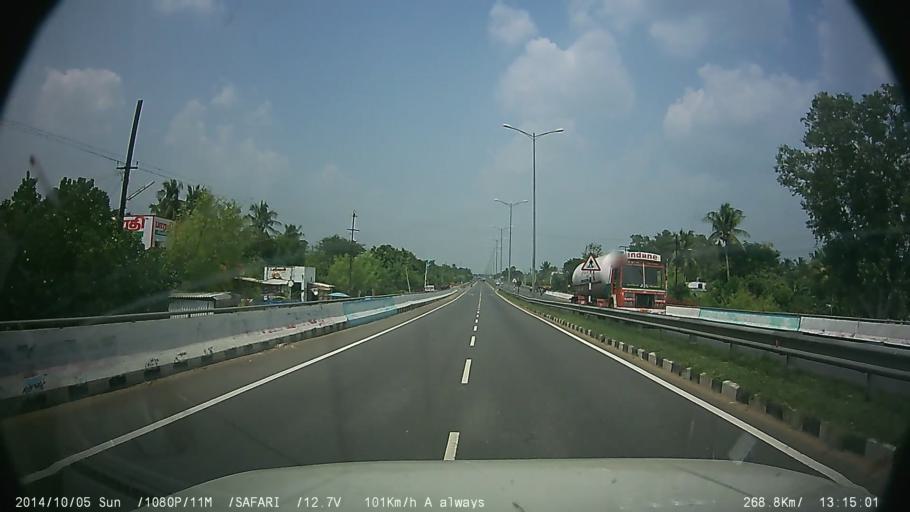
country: IN
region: Tamil Nadu
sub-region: Villupuram
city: Villupuram
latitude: 11.9864
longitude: 79.5112
